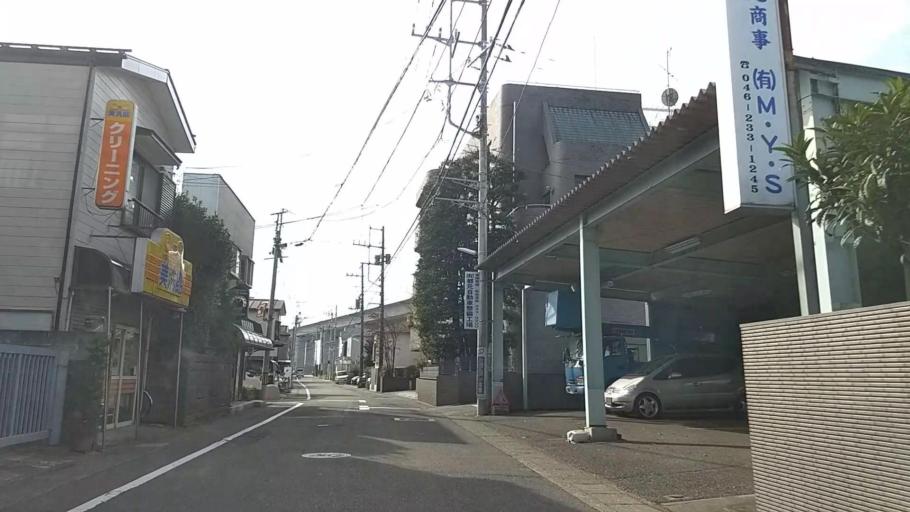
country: JP
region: Kanagawa
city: Atsugi
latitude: 35.4488
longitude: 139.3743
